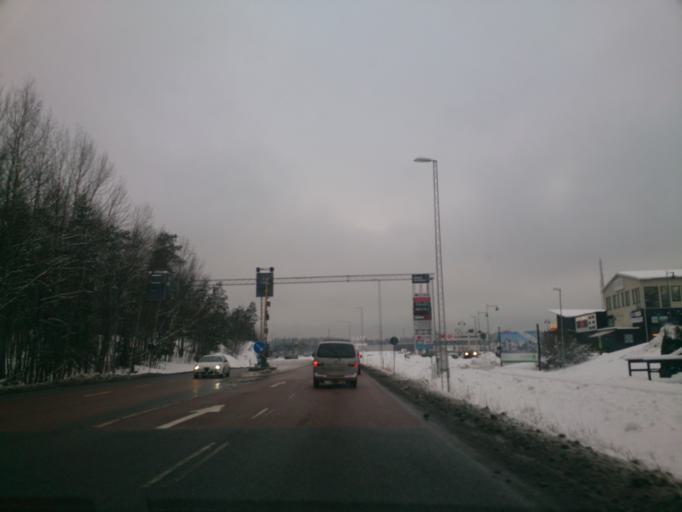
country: SE
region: Stockholm
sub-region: Varmdo Kommun
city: Mortnas
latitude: 59.3122
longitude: 18.4331
